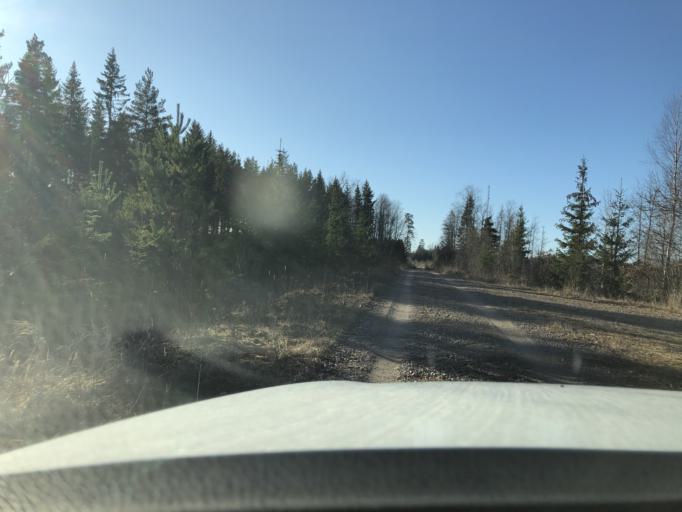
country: SE
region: Gaevleborg
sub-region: Gavle Kommun
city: Hedesunda
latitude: 60.3020
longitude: 16.8927
